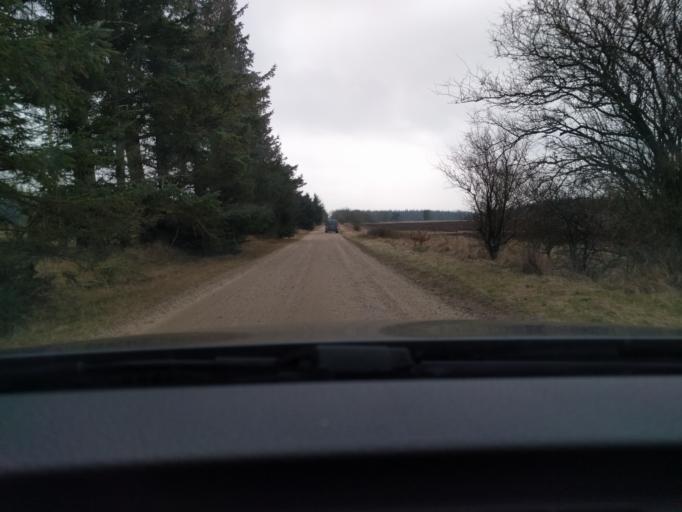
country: DK
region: Central Jutland
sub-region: Skive Kommune
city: Skive
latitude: 56.5008
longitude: 8.9374
